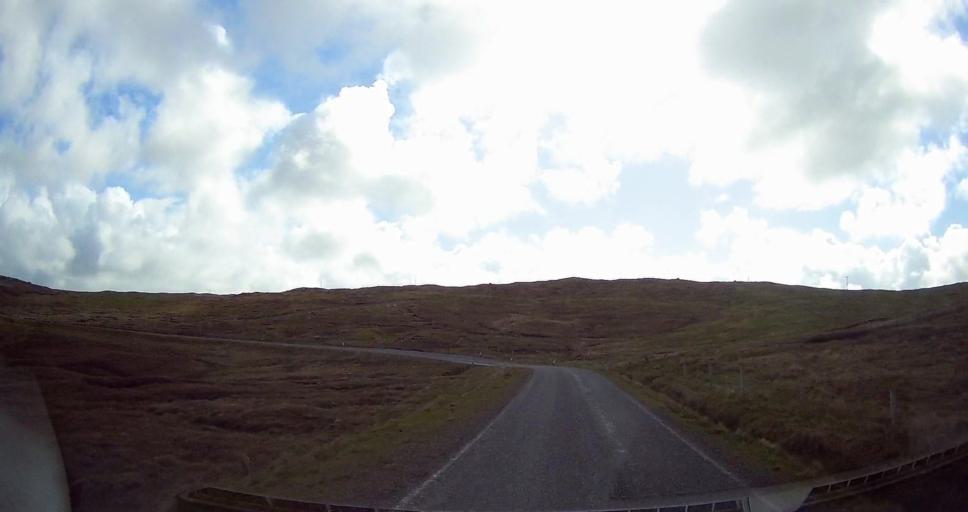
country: GB
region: Scotland
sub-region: Shetland Islands
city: Lerwick
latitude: 60.4869
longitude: -1.3941
